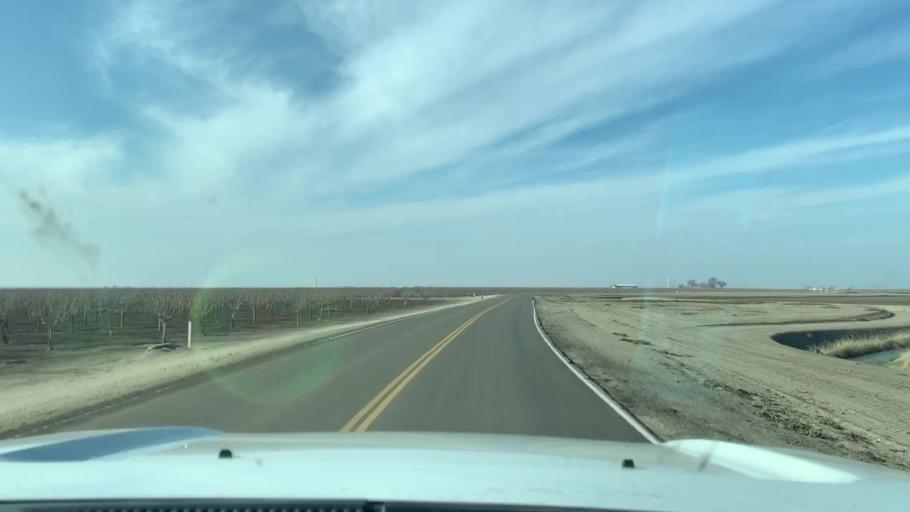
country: US
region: California
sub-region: Kern County
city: Buttonwillow
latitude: 35.4483
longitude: -119.5596
